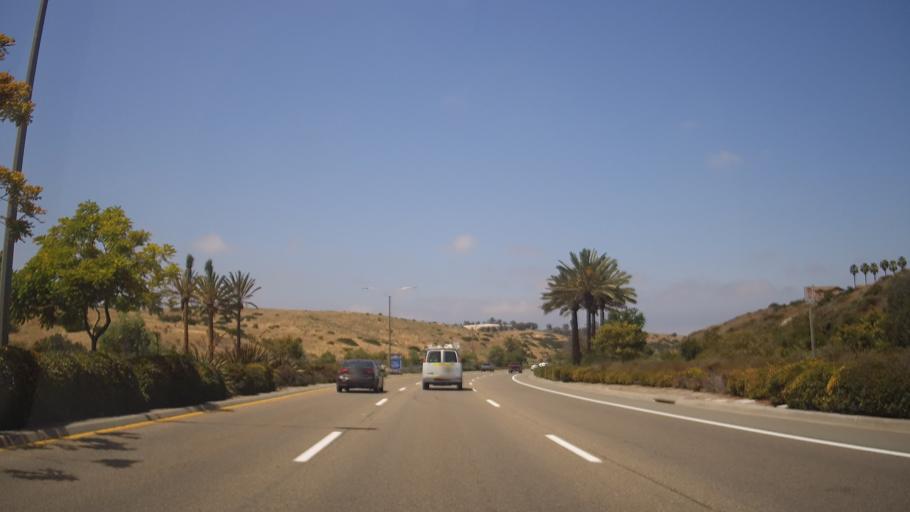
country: US
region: California
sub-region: San Diego County
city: Bonita
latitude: 32.6121
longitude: -117.0112
